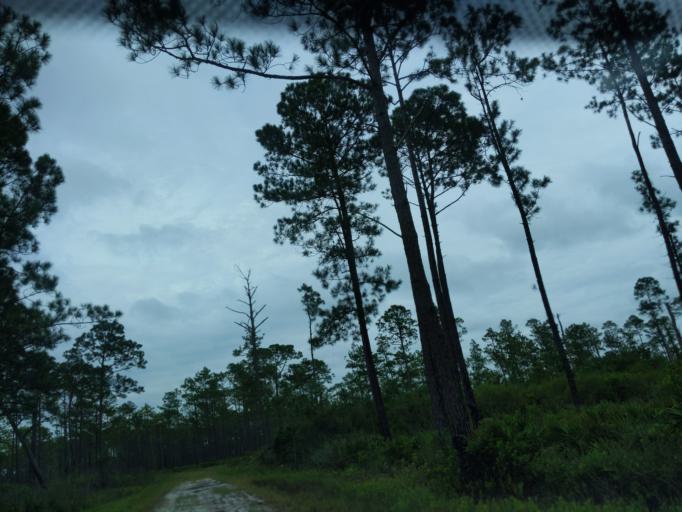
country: US
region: Florida
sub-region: Gadsden County
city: Midway
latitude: 30.3534
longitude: -84.4876
